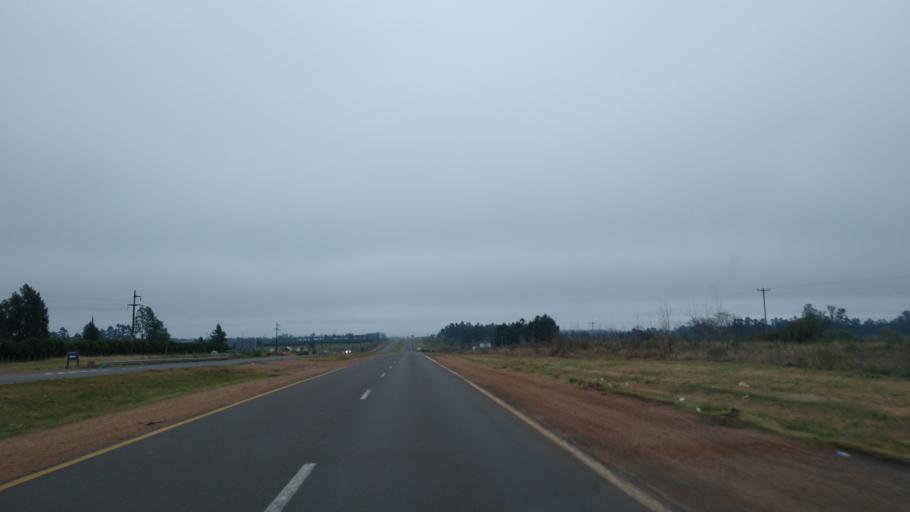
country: AR
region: Entre Rios
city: Chajari
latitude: -30.8187
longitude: -58.0435
